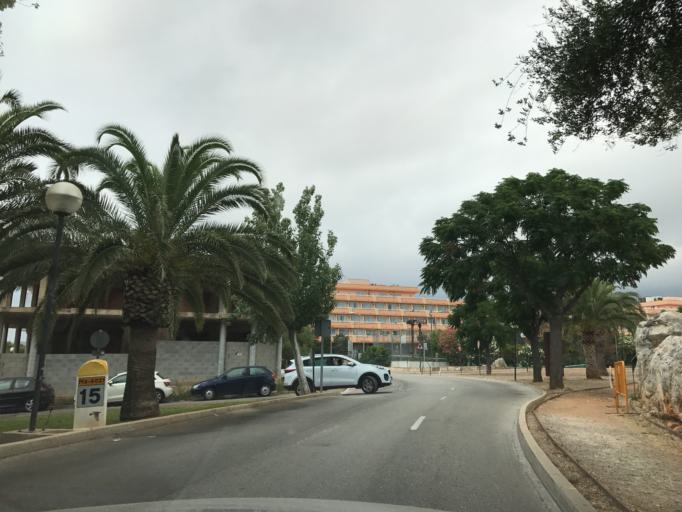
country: ES
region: Balearic Islands
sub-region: Illes Balears
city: Son Servera
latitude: 39.5682
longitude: 3.3720
